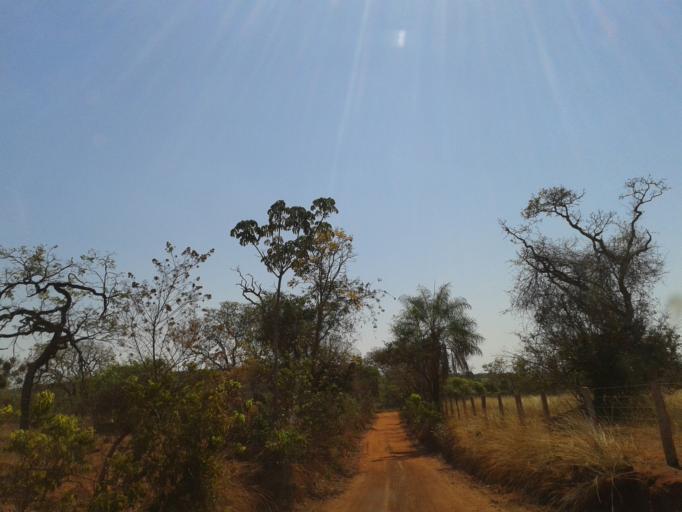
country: BR
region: Minas Gerais
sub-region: Ituiutaba
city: Ituiutaba
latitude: -19.0813
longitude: -49.3066
